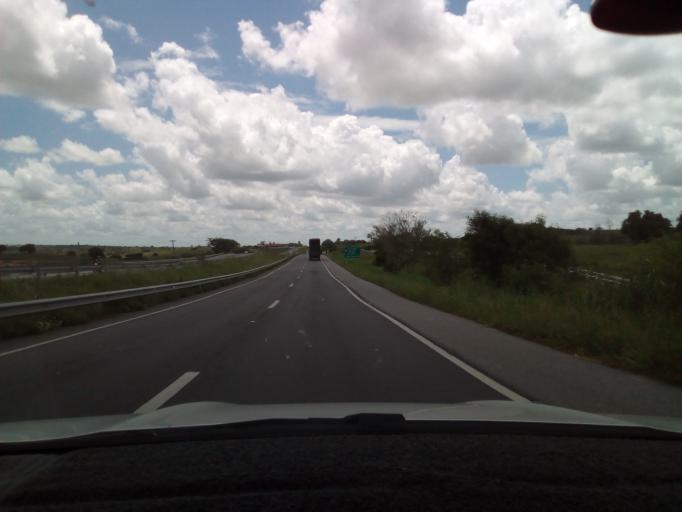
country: BR
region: Paraiba
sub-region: Gurinhem
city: Gurinhem
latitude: -7.1708
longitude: -35.3820
